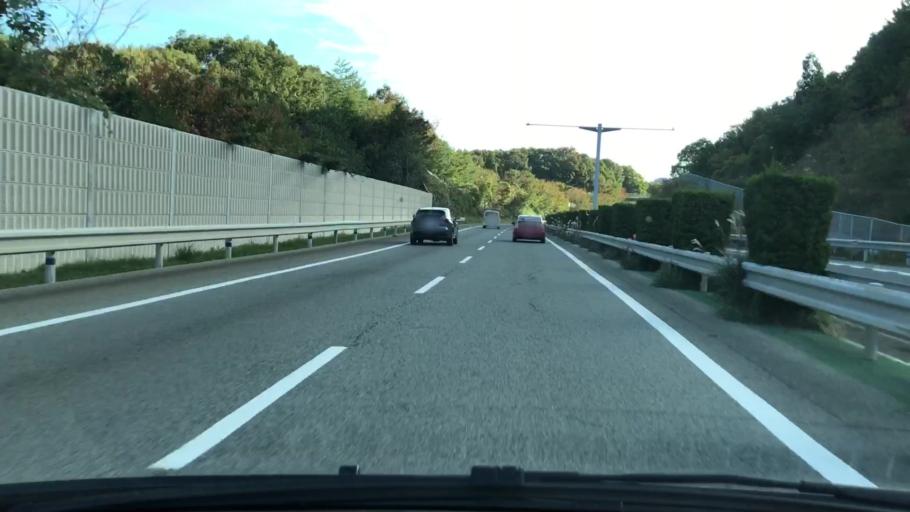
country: JP
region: Hyogo
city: Kobe
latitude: 34.7623
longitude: 135.1867
